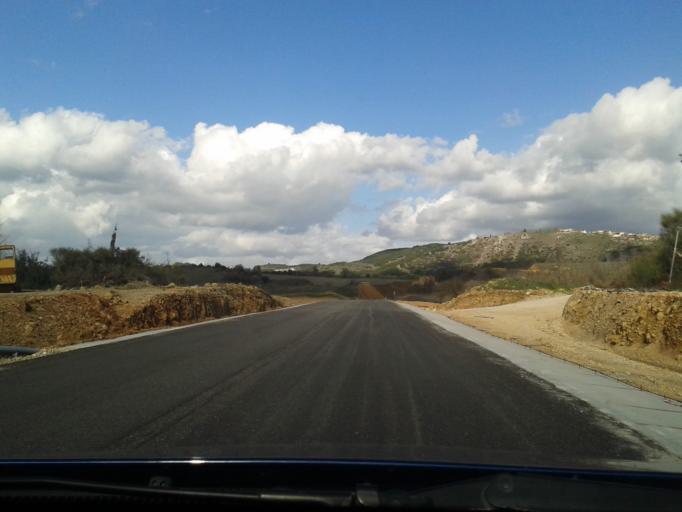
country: GR
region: West Greece
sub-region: Nomos Aitolias kai Akarnanias
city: Fitiai
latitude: 38.6837
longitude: 21.1681
